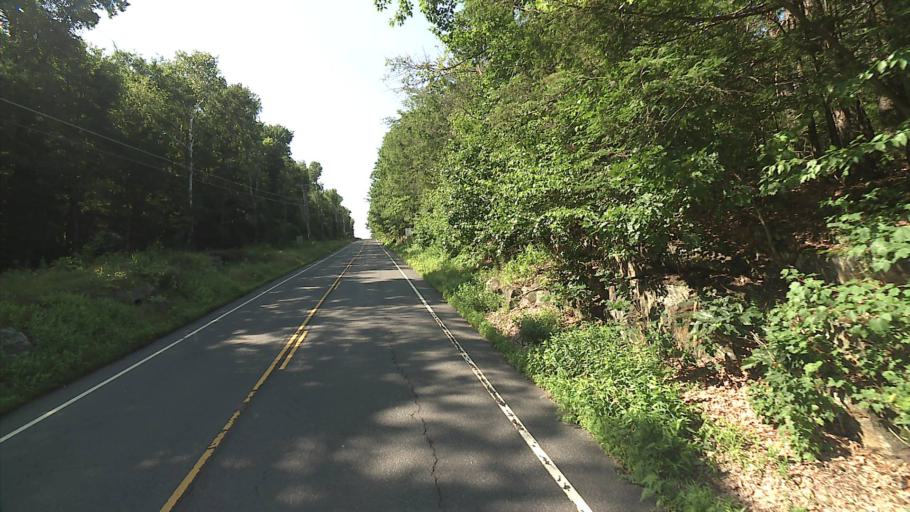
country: US
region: Massachusetts
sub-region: Hampden County
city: Granville
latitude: 42.0242
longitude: -72.9671
